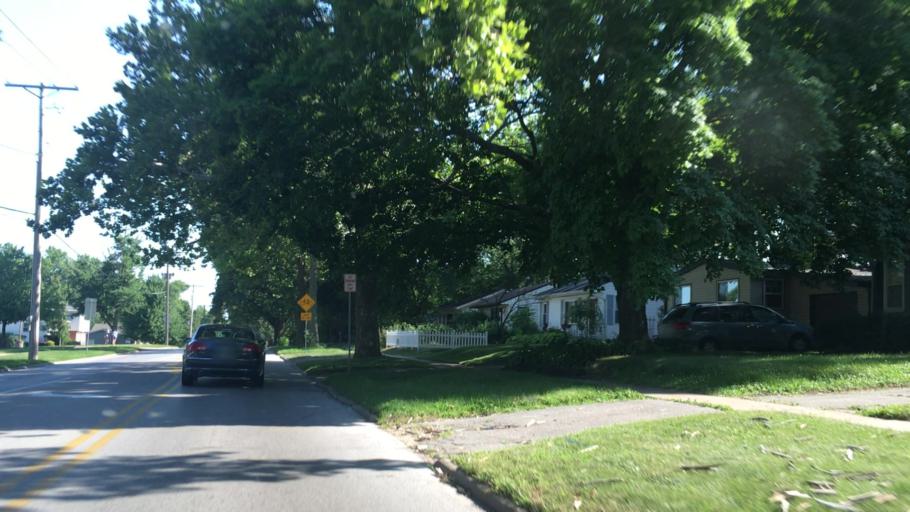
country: US
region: Iowa
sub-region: Johnson County
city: Iowa City
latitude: 41.6565
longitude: -91.5020
